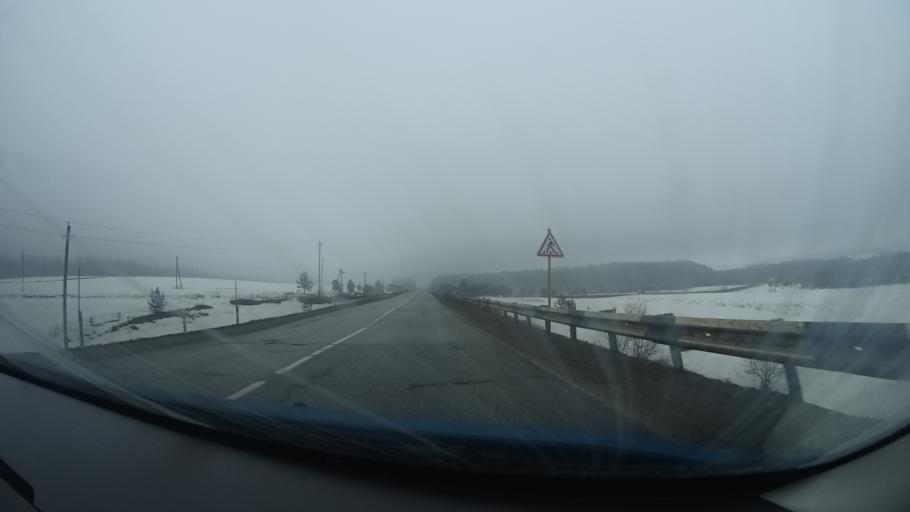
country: RU
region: Perm
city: Kuyeda
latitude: 56.4726
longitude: 55.7486
